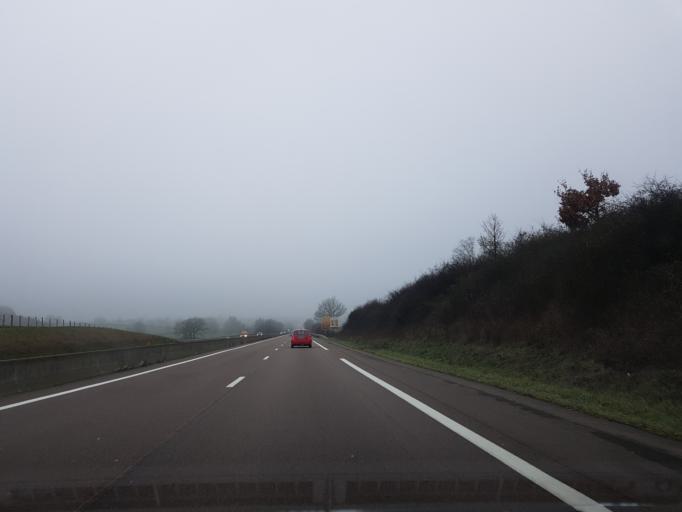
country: FR
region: Bourgogne
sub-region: Departement de Saone-et-Loire
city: Ecuisses
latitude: 46.7449
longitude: 4.5271
